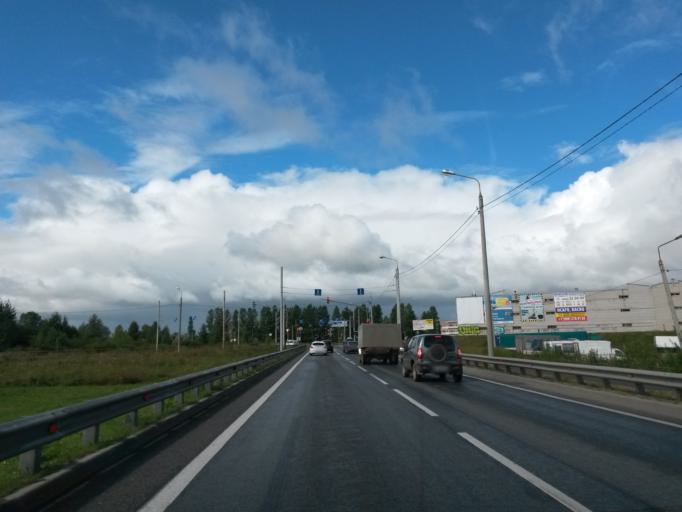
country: RU
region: Jaroslavl
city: Yaroslavl
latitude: 57.6712
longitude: 39.7763
